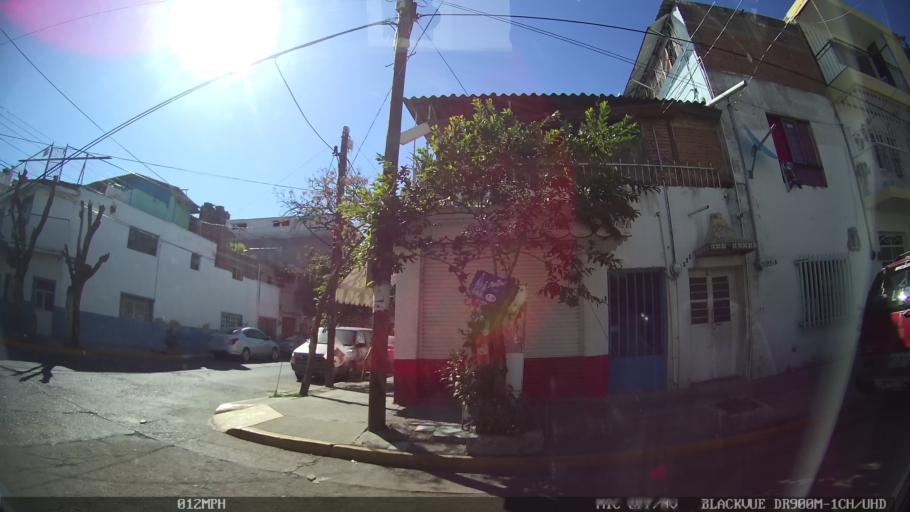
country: MX
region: Jalisco
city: Tlaquepaque
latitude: 20.6722
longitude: -103.2833
